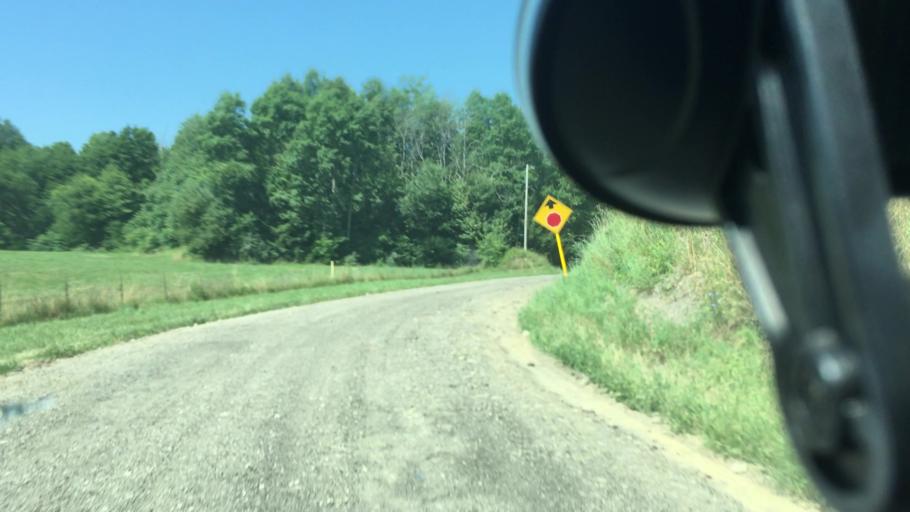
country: US
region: Ohio
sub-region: Columbiana County
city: Lisbon
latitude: 40.7626
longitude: -80.7921
